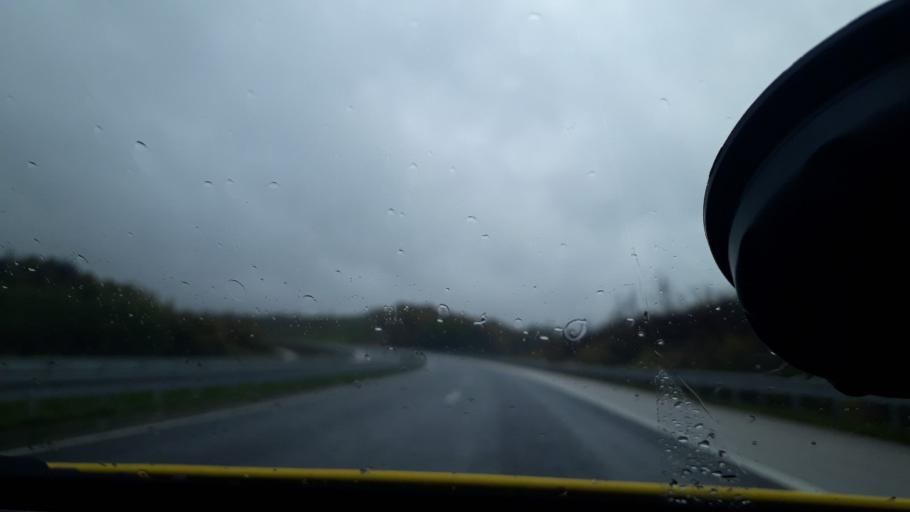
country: BA
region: Republika Srpska
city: Derventa
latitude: 44.8447
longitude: 17.9673
